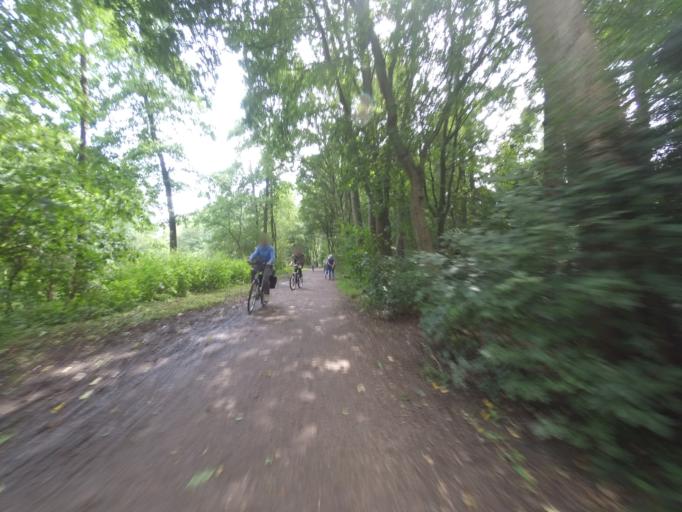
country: DE
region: Schleswig-Holstein
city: Oststeinbek
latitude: 53.5552
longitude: 10.1350
